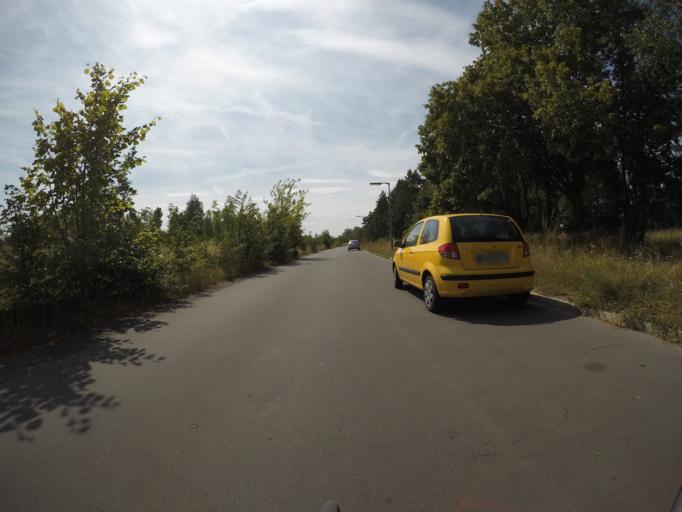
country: DE
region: Berlin
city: Marienfelde
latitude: 52.3958
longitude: 13.3759
